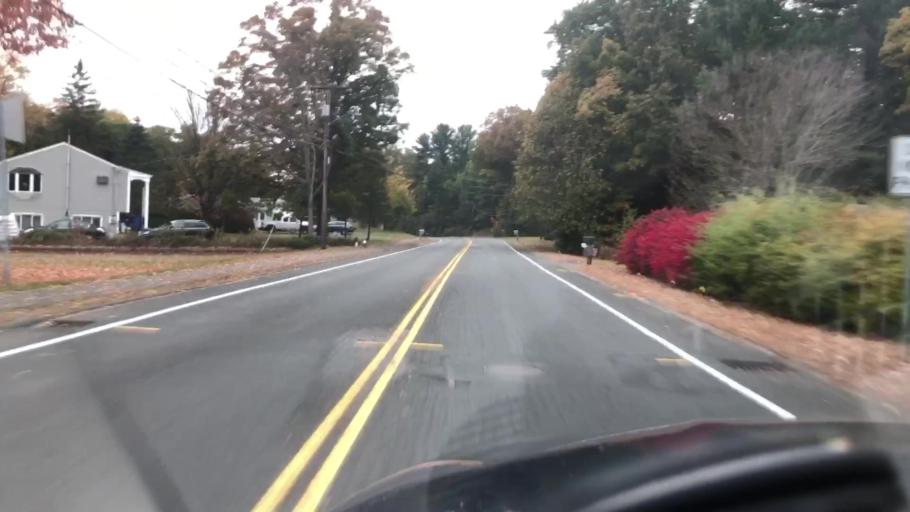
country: US
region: Massachusetts
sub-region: Hampshire County
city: Easthampton
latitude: 42.2397
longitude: -72.6861
